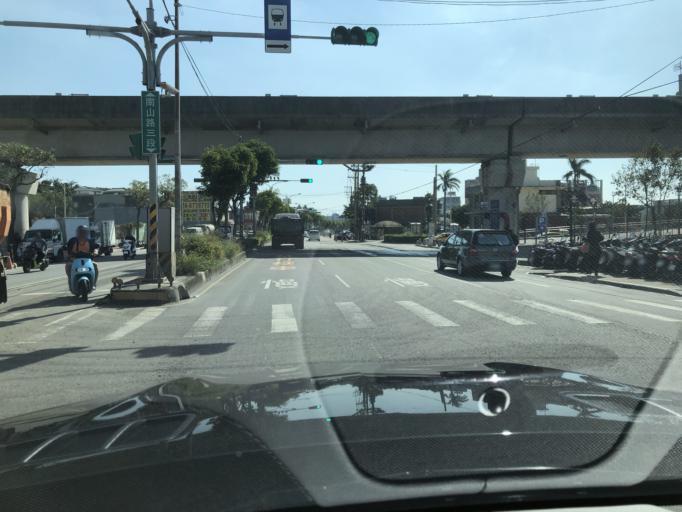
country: TW
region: Taiwan
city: Taoyuan City
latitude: 25.0813
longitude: 121.2859
